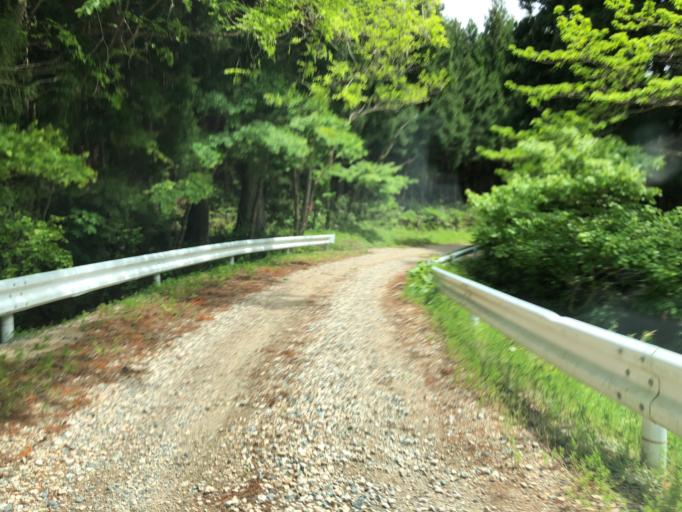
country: JP
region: Miyagi
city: Marumori
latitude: 37.7356
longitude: 140.8293
